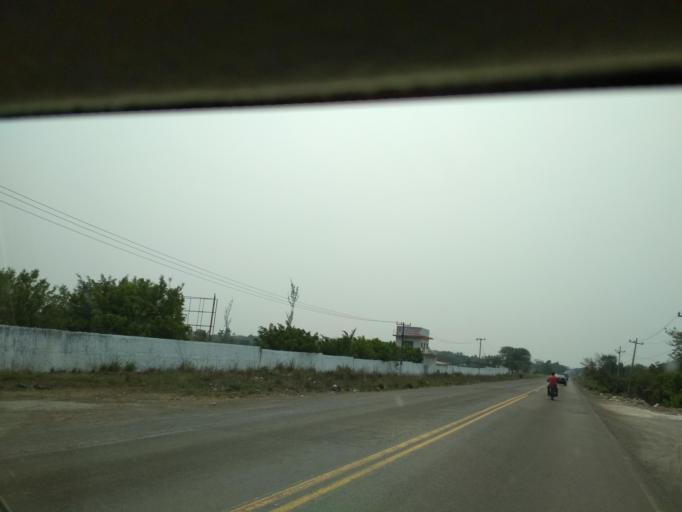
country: MX
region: Veracruz
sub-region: Veracruz
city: Delfino Victoria (Santa Fe)
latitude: 19.1947
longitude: -96.2902
